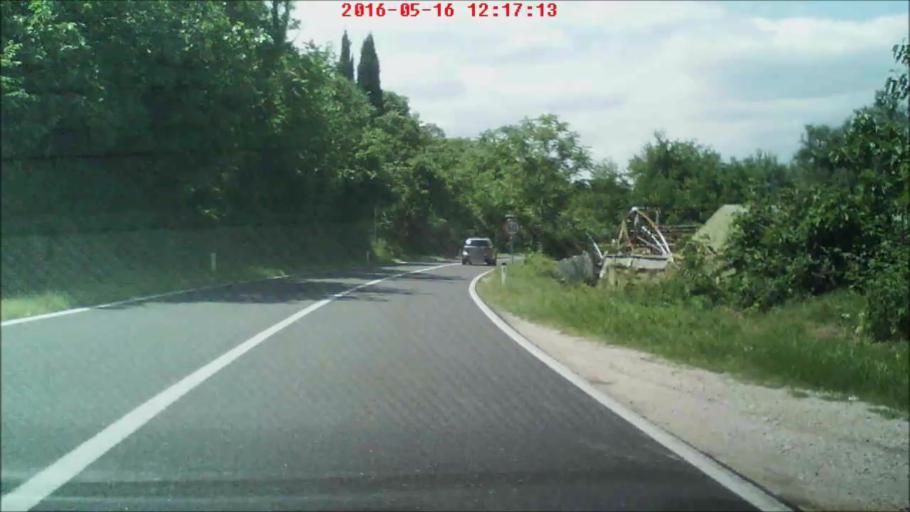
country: HR
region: Dubrovacko-Neretvanska
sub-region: Grad Dubrovnik
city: Metkovic
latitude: 43.0524
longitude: 17.6947
